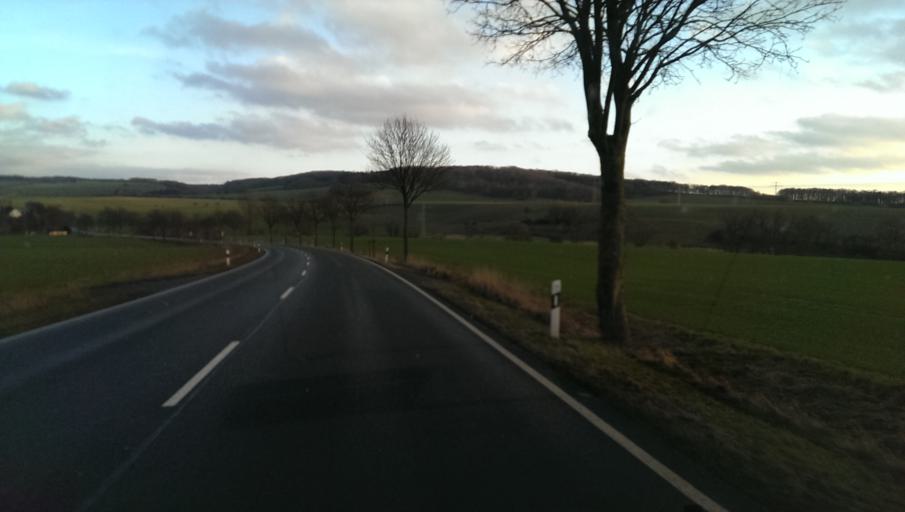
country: DE
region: Lower Saxony
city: Einbeck
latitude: 51.8653
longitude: 9.8468
